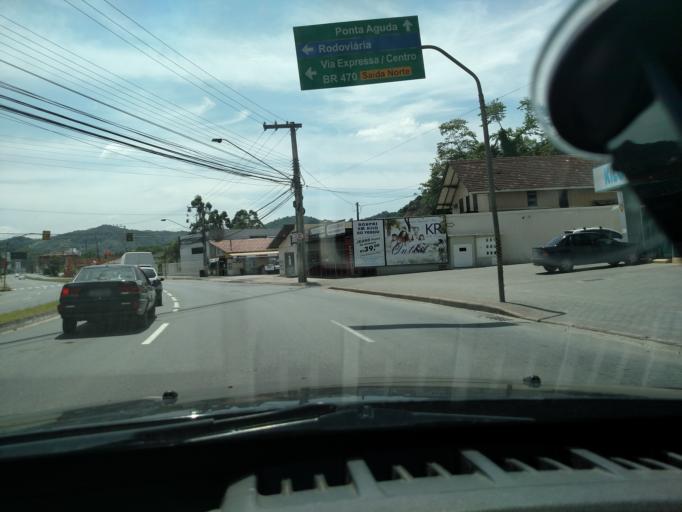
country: BR
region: Santa Catarina
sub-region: Blumenau
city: Blumenau
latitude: -26.8974
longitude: -49.0723
